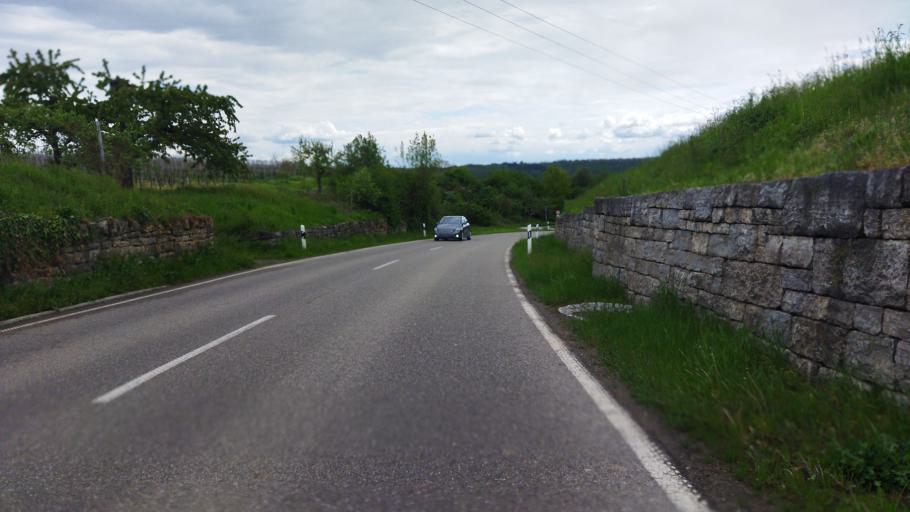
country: DE
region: Baden-Wuerttemberg
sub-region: Regierungsbezirk Stuttgart
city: Hessigheim
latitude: 49.0053
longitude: 9.1879
